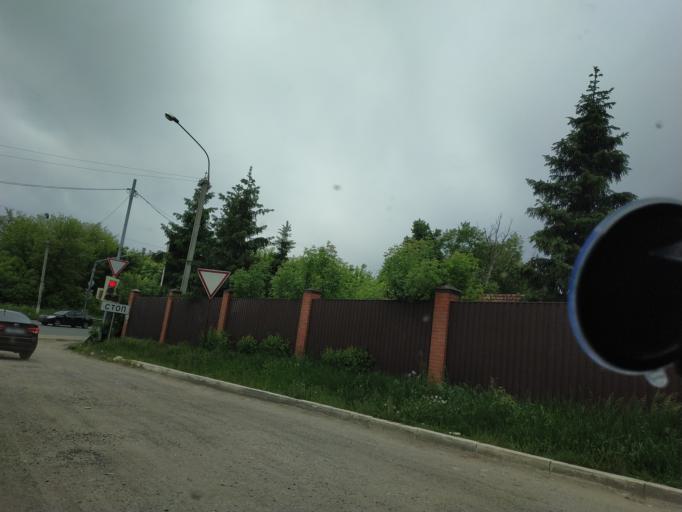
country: RU
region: Moskovskaya
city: Zhukovskiy
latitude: 55.5477
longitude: 38.0696
